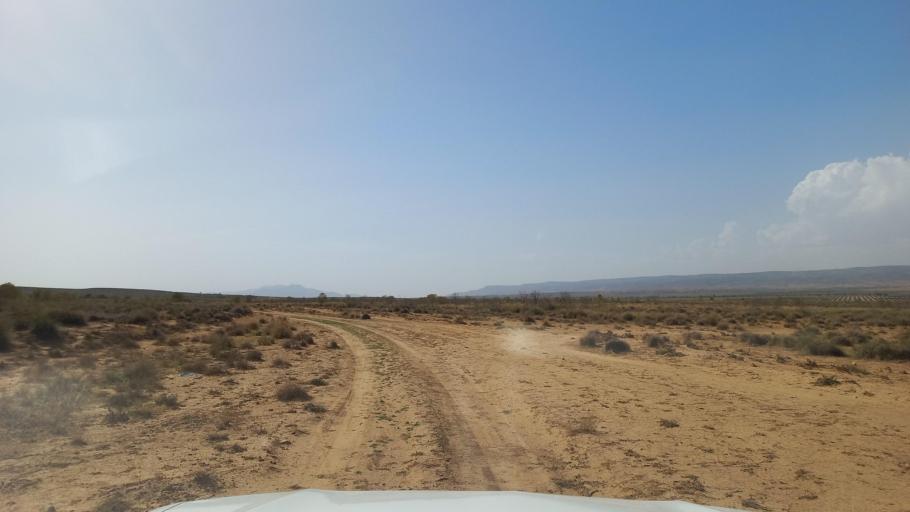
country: TN
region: Al Qasrayn
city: Kasserine
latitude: 35.2149
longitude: 9.0136
